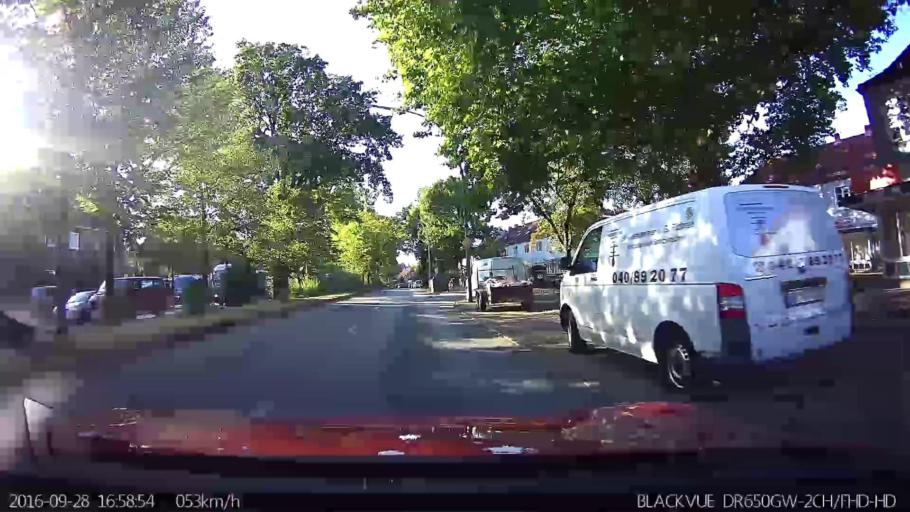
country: DE
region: Hamburg
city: Eidelstedt
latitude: 53.5667
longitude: 9.8934
